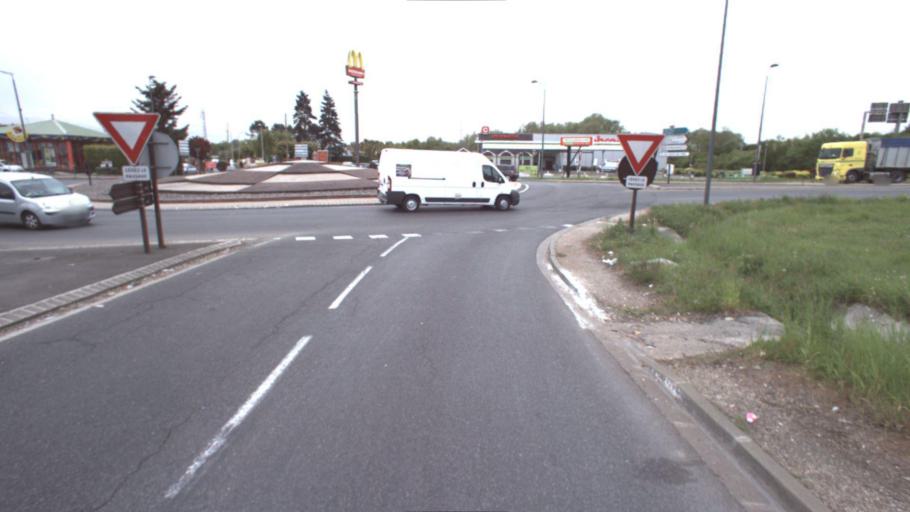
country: FR
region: Ile-de-France
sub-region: Departement de Seine-et-Marne
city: Servon
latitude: 48.7028
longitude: 2.5976
